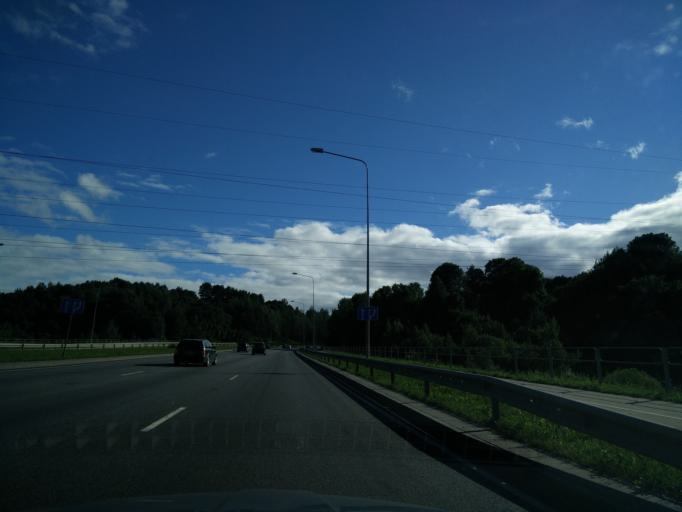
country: LT
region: Vilnius County
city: Lazdynai
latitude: 54.6654
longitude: 25.1732
